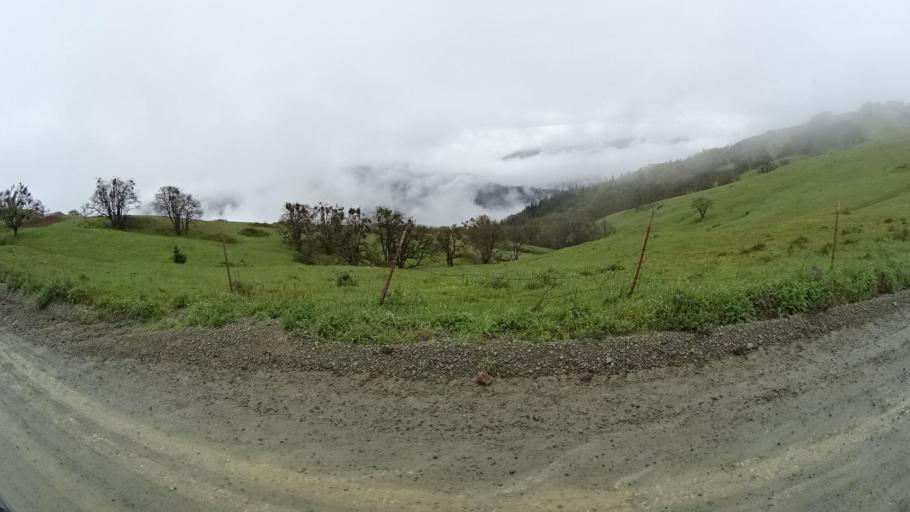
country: US
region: California
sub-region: Humboldt County
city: Westhaven-Moonstone
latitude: 41.1479
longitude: -123.8926
